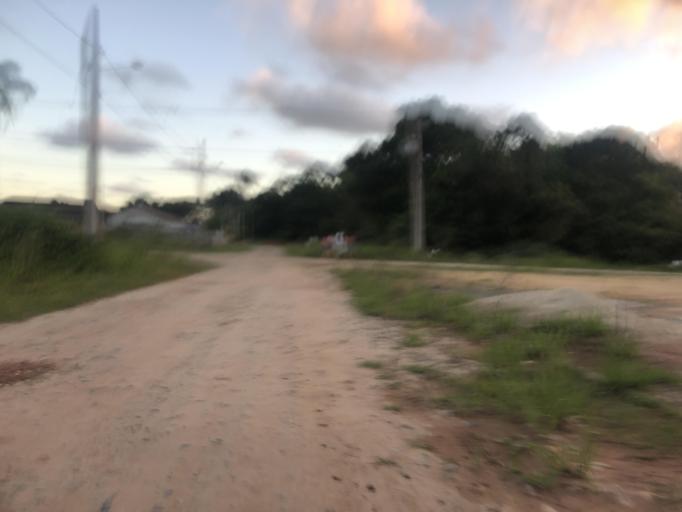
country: BR
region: Santa Catarina
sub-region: Sao Francisco Do Sul
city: Sao Francisco do Sul
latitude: -26.2218
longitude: -48.5338
